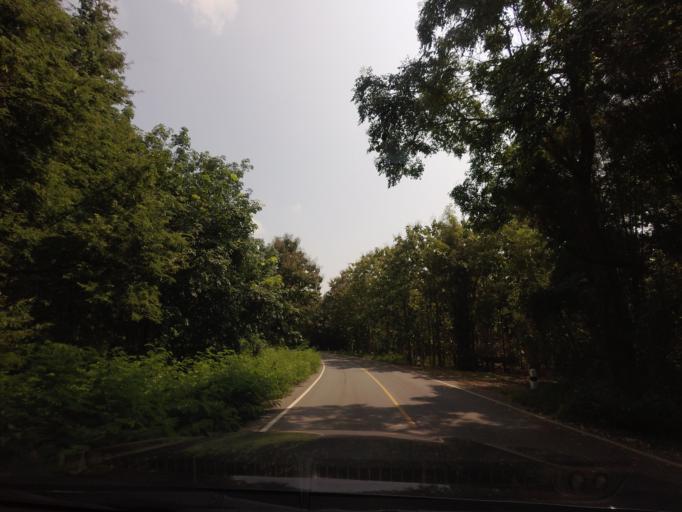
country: TH
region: Nan
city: Nan
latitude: 18.8510
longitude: 100.7841
